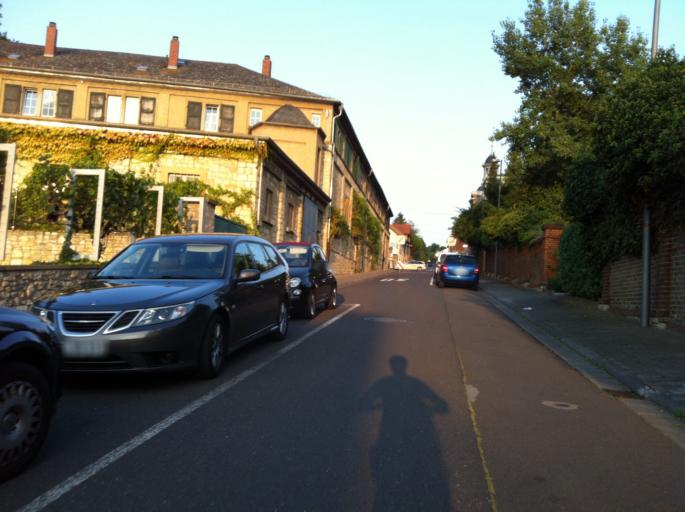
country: DE
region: Rheinland-Pfalz
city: Ingelheim am Rhein
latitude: 49.9669
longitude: 8.0574
